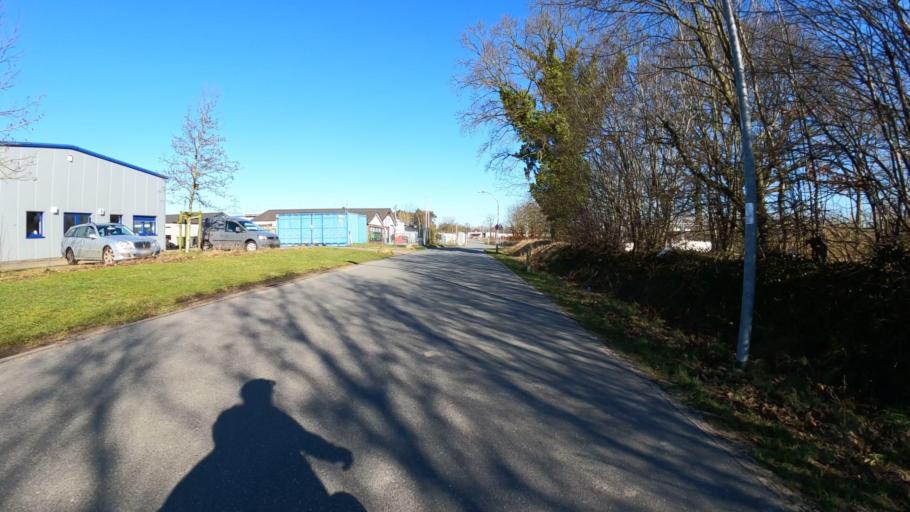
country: DE
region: Schleswig-Holstein
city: Kummerfeld
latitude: 53.6862
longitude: 9.7830
